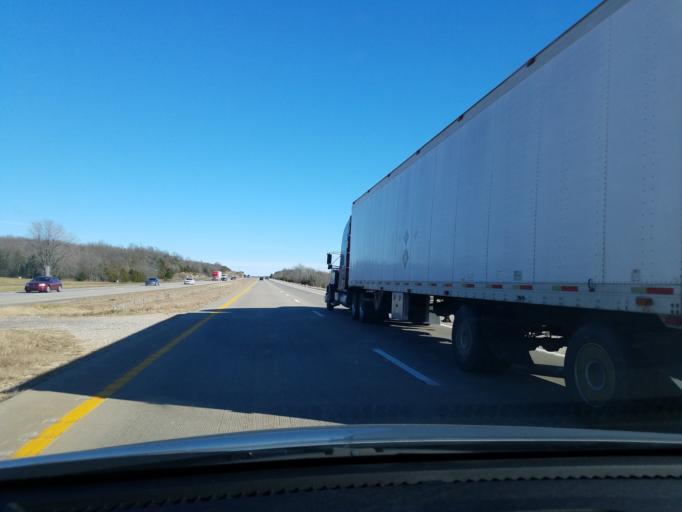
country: US
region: Missouri
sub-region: Laclede County
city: Lebanon
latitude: 37.7547
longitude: -92.5571
